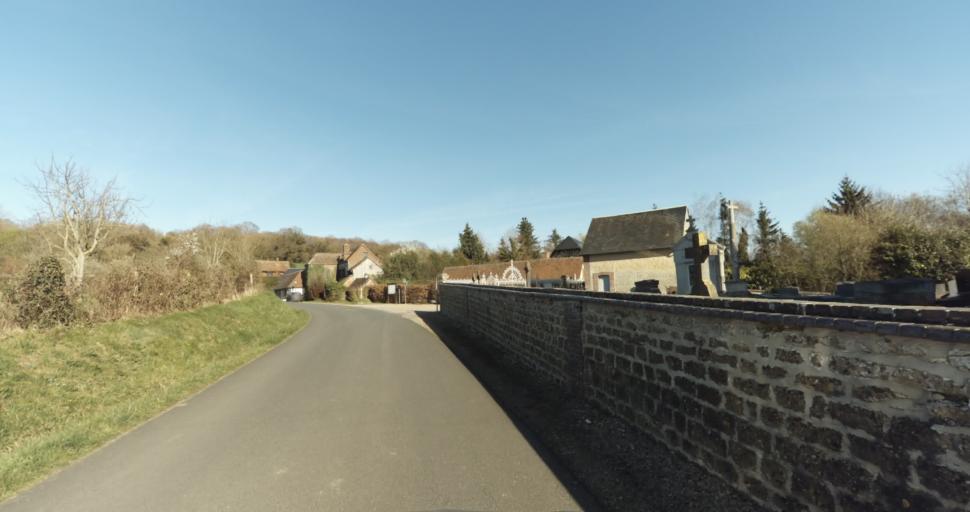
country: FR
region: Lower Normandy
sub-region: Departement du Calvados
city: Saint-Pierre-sur-Dives
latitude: 49.0398
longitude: 0.0384
